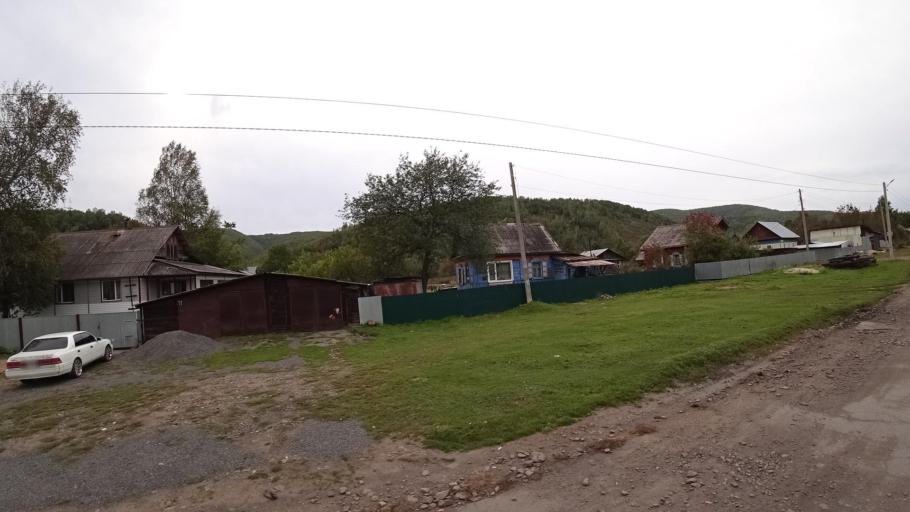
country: RU
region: Jewish Autonomous Oblast
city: Khingansk
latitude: 49.0250
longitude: 131.0480
